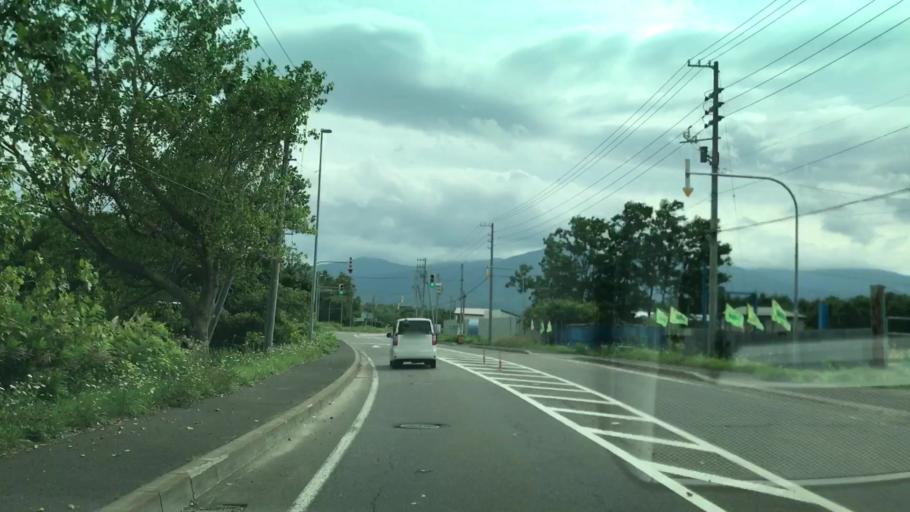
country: JP
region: Hokkaido
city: Iwanai
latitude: 43.0074
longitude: 140.5427
